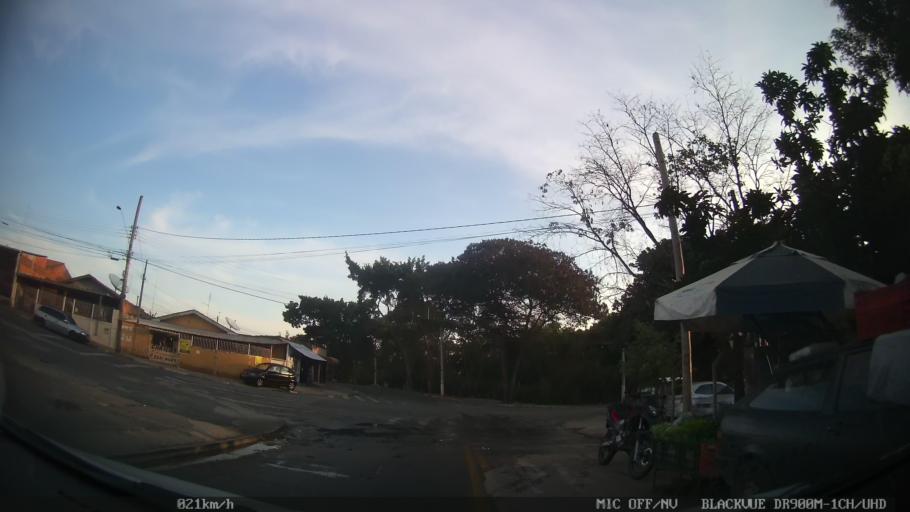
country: BR
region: Sao Paulo
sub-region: Campinas
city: Campinas
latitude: -22.9769
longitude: -47.1403
